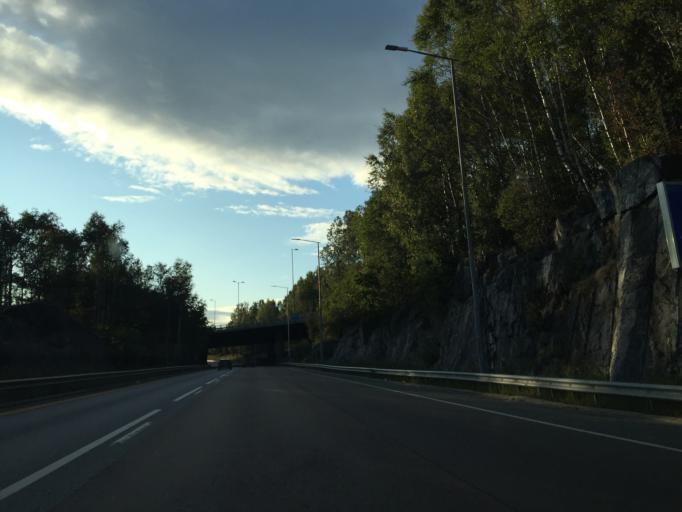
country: NO
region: Akershus
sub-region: Lorenskog
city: Kjenn
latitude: 59.9384
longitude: 10.9312
